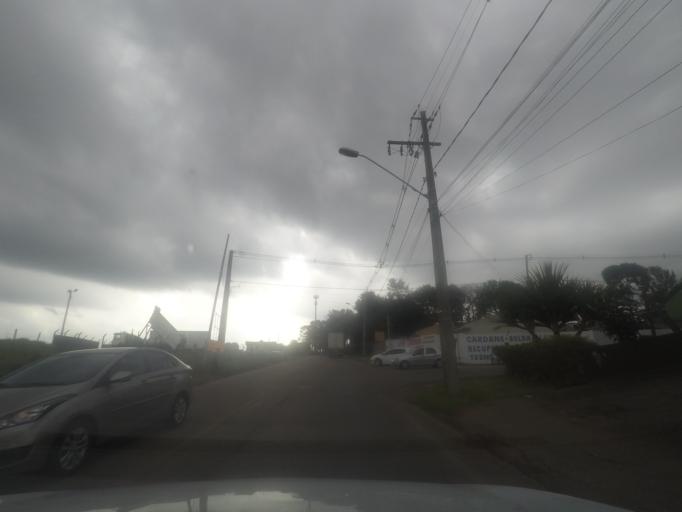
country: BR
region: Parana
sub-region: Sao Jose Dos Pinhais
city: Sao Jose dos Pinhais
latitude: -25.5519
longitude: -49.2779
